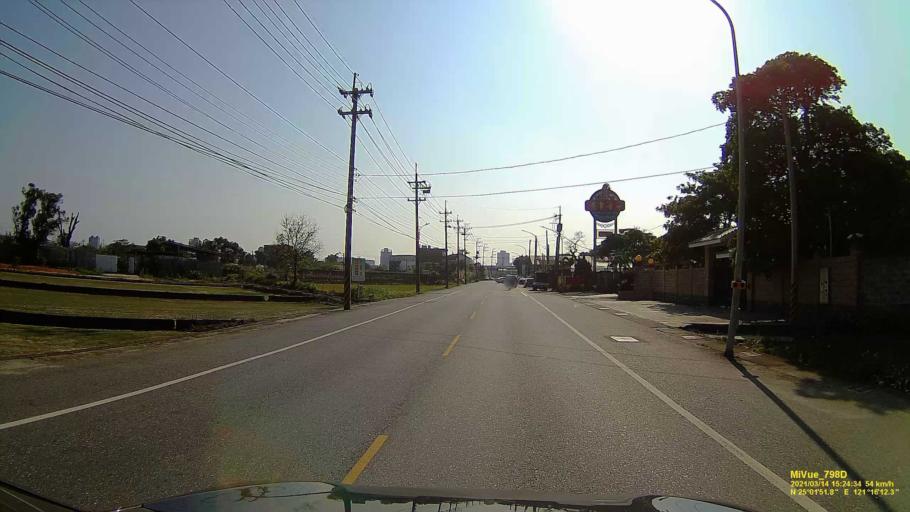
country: TW
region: Taiwan
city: Taoyuan City
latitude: 25.0308
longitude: 121.2698
